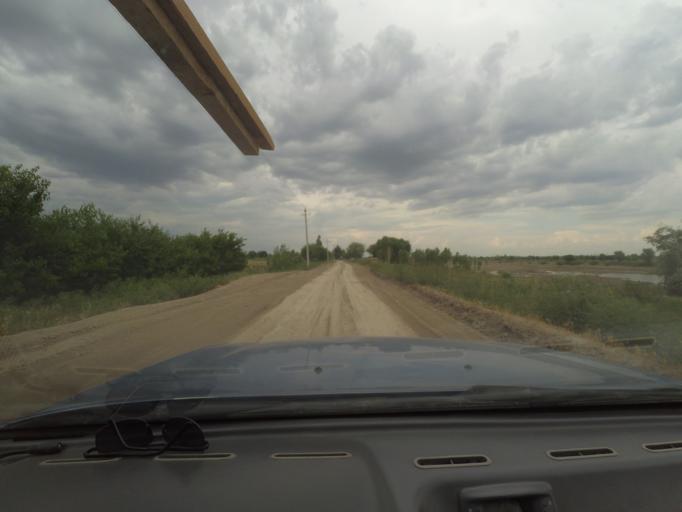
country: TJ
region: Viloyati Sughd
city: Buston
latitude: 40.5465
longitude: 69.0785
